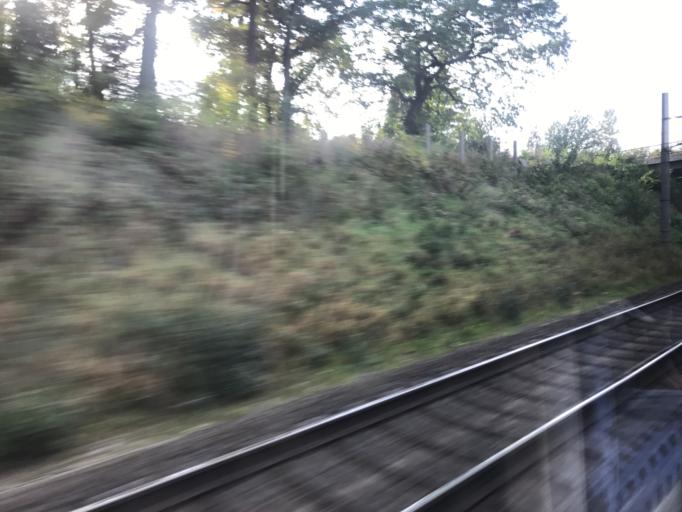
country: DE
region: Saxony
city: Weissig
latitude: 51.2690
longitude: 13.4678
